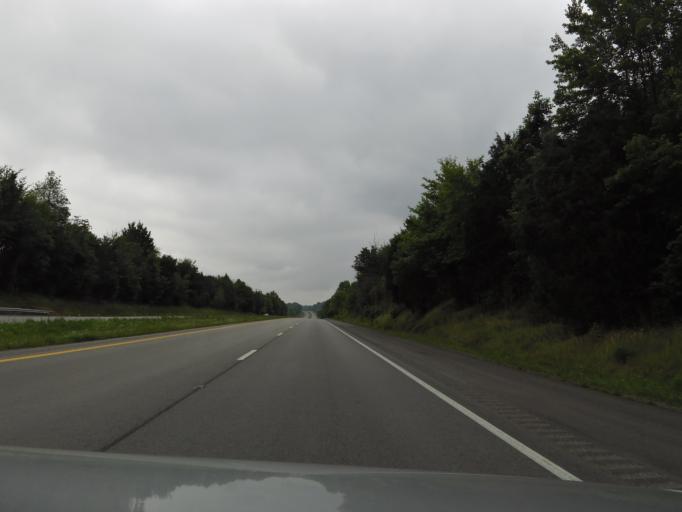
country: US
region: Kentucky
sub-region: Grayson County
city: Leitchfield
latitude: 37.4110
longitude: -86.4382
